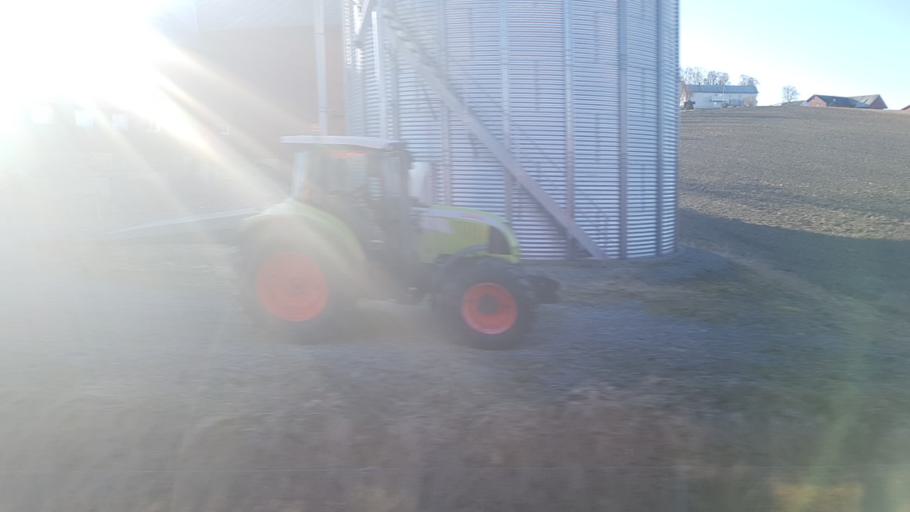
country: NO
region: Nord-Trondelag
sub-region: Levanger
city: Skogn
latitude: 63.6932
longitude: 11.1781
